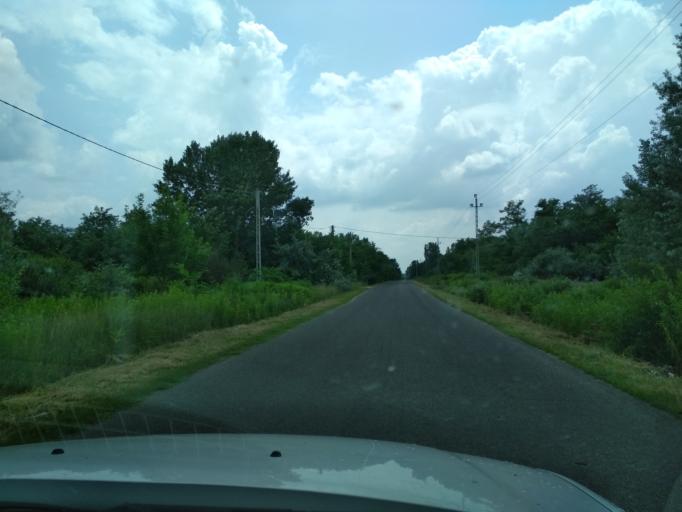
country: HU
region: Pest
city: Nagykata
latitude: 47.3943
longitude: 19.7581
